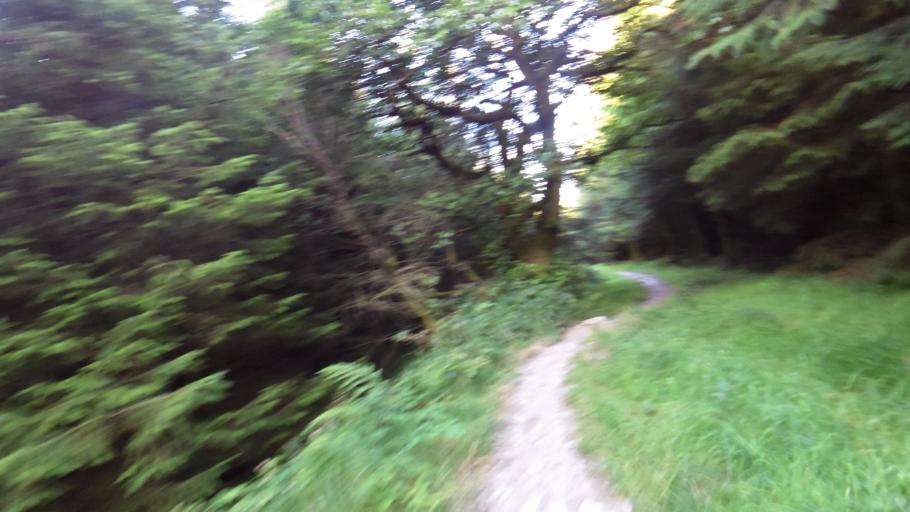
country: GB
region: England
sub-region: Lancashire
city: Clitheroe
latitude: 54.0027
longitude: -2.4019
